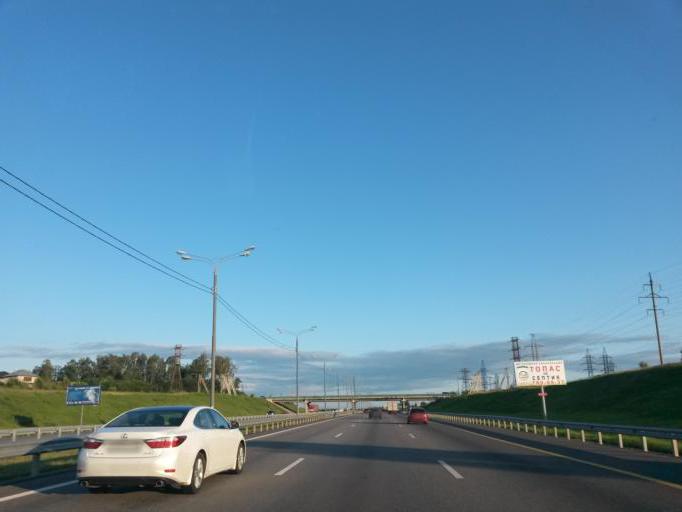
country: RU
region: Moskovskaya
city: Vostryakovo
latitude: 55.3805
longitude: 37.7777
